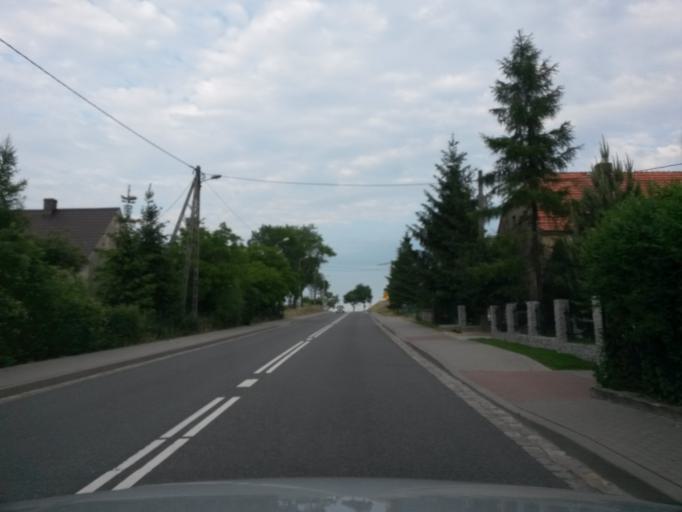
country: PL
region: Lower Silesian Voivodeship
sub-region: Powiat sredzki
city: Udanin
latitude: 50.9869
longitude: 16.4307
